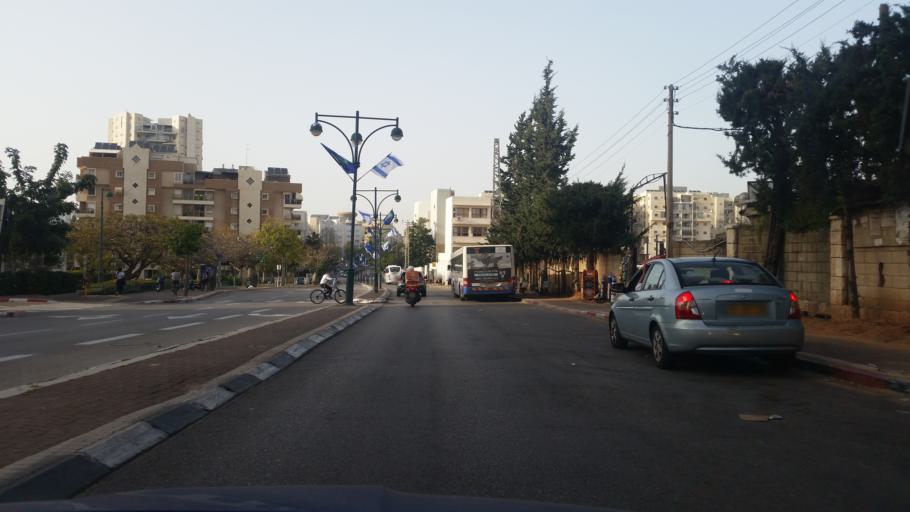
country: IL
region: Tel Aviv
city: Bene Beraq
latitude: 32.0726
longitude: 34.8330
